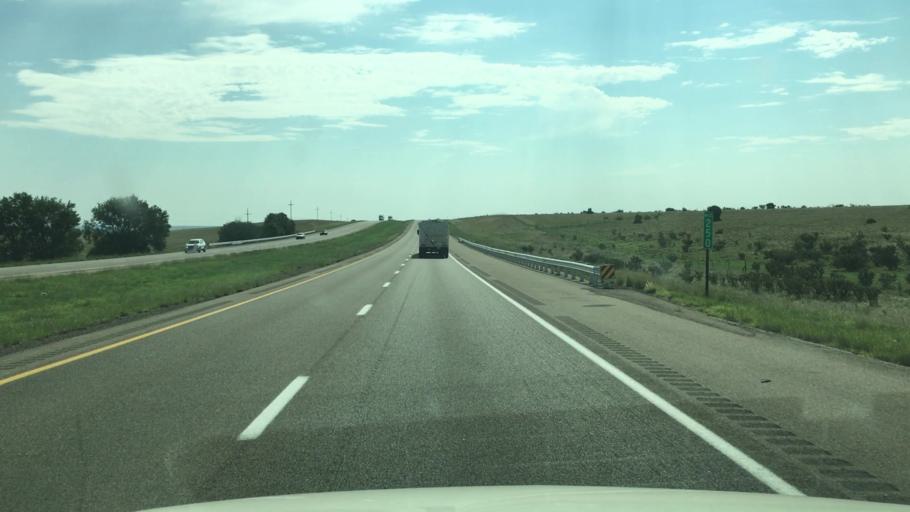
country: US
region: New Mexico
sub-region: Guadalupe County
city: Santa Rosa
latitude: 34.9821
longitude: -105.1058
